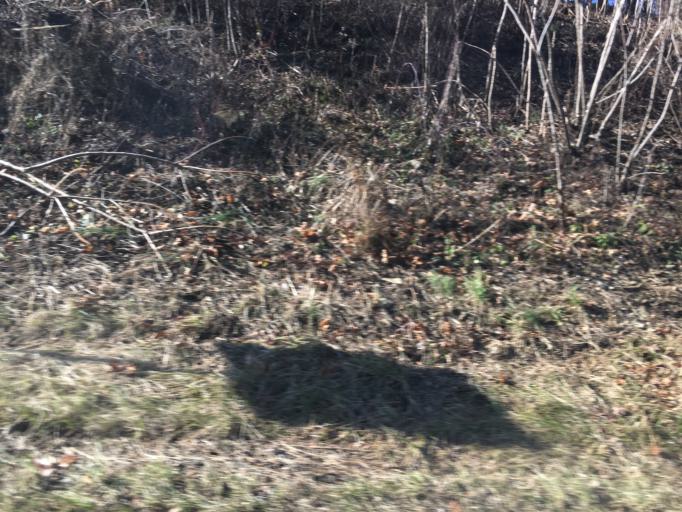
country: US
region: Pennsylvania
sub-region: Lehigh County
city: Allentown
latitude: 40.6195
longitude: -75.5360
